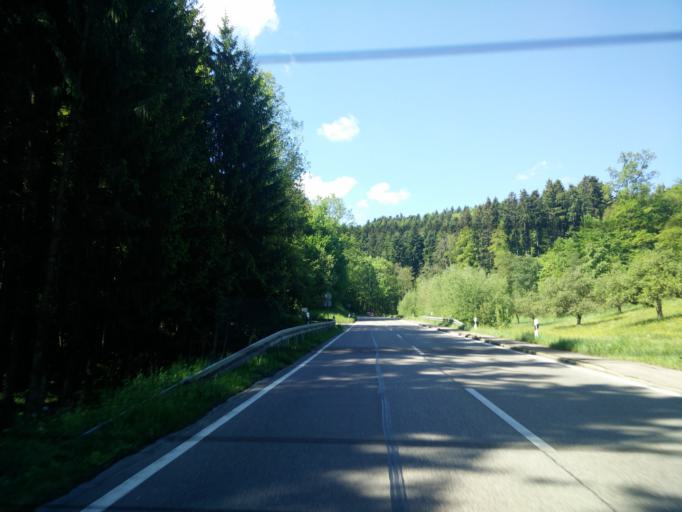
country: DE
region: Baden-Wuerttemberg
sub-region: Regierungsbezirk Stuttgart
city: Gaildorf
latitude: 48.9740
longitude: 9.7698
